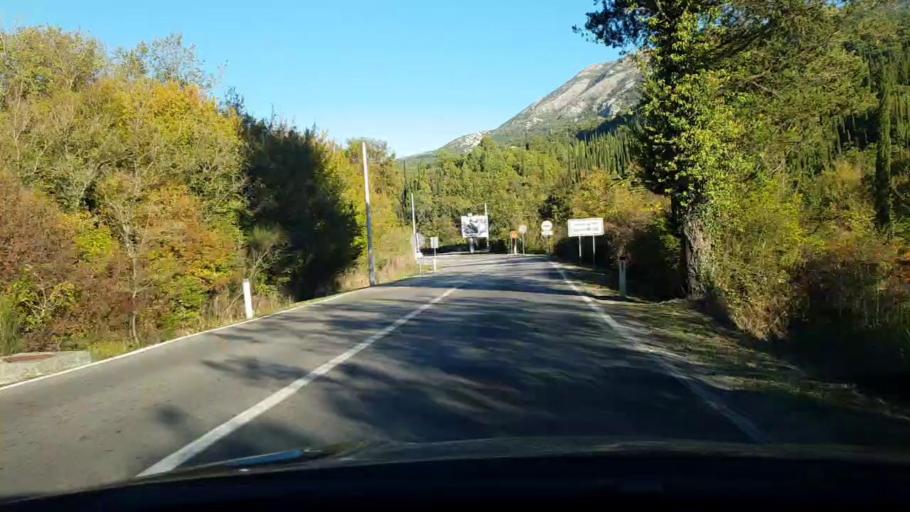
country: ME
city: Igalo
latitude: 42.4801
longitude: 18.4580
